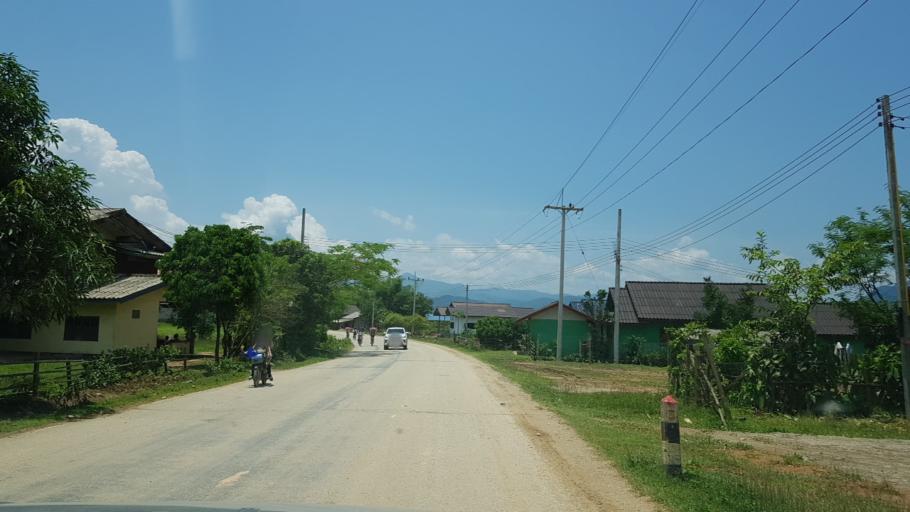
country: LA
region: Vientiane
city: Muang Kasi
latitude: 19.2642
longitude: 102.2314
